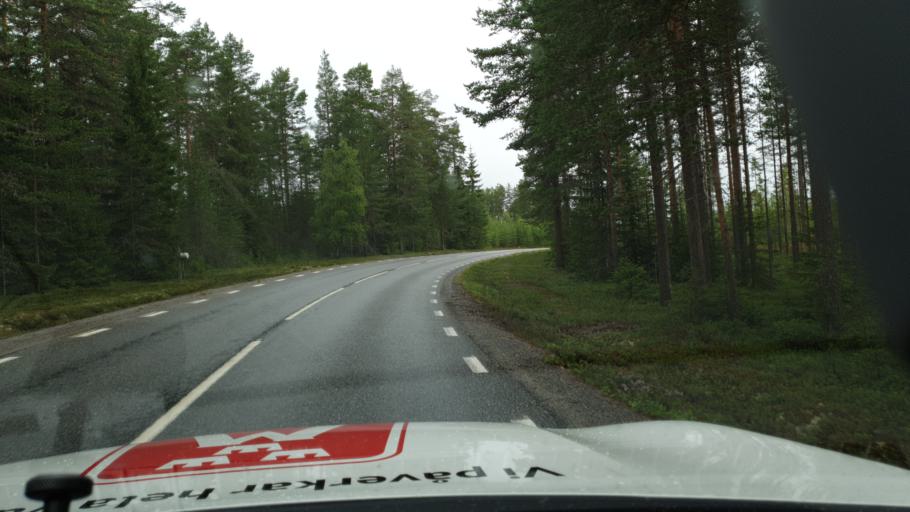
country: SE
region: Vaesterbotten
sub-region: Umea Kommun
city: Saevar
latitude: 64.0201
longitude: 20.4868
